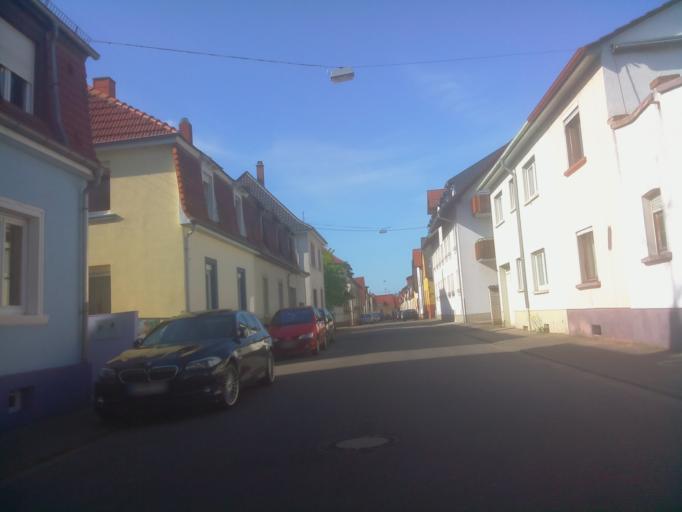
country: DE
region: Baden-Wuerttemberg
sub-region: Karlsruhe Region
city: Edingen-Neckarhausen
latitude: 49.4651
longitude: 8.5979
